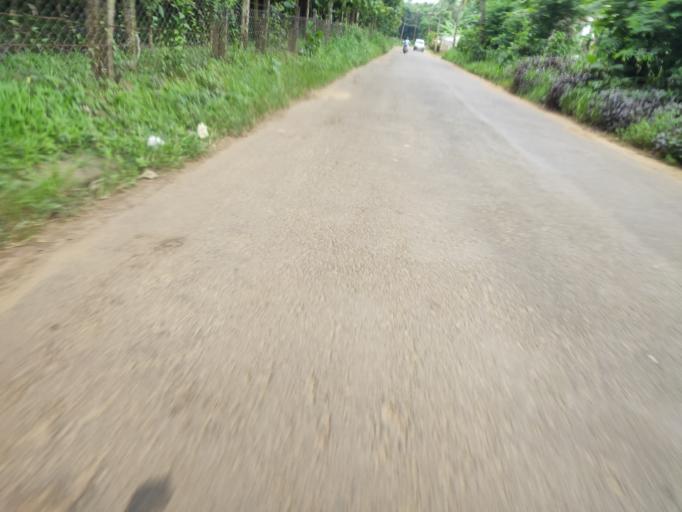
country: IN
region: Kerala
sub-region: Malappuram
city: Manjeri
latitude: 11.2419
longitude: 76.2870
